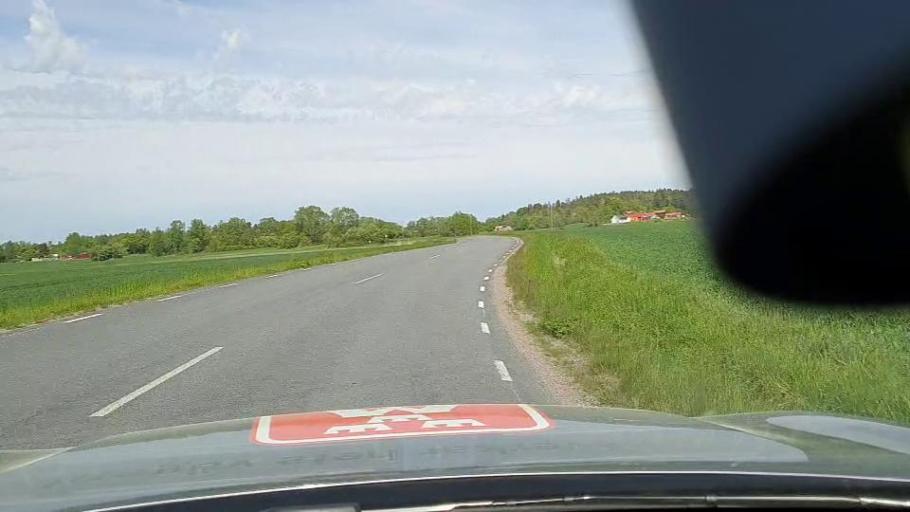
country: SE
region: Soedermanland
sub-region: Eskilstuna Kommun
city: Skogstorp
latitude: 59.3105
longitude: 16.4635
